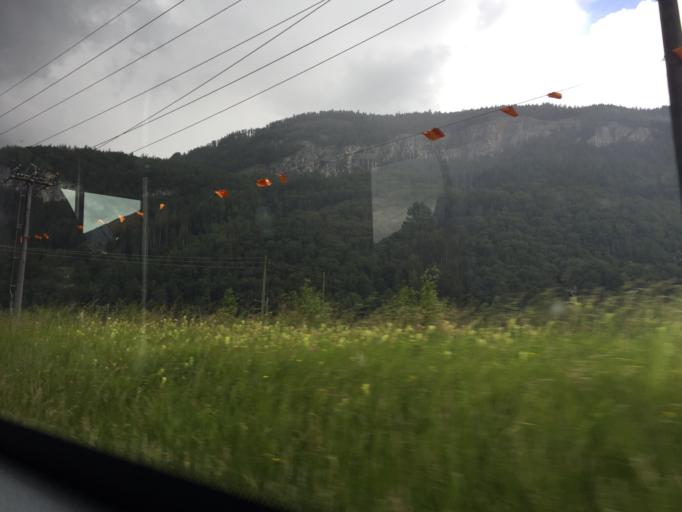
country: CH
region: Bern
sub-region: Interlaken-Oberhasli District
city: Meiringen
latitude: 46.7403
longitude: 8.1482
